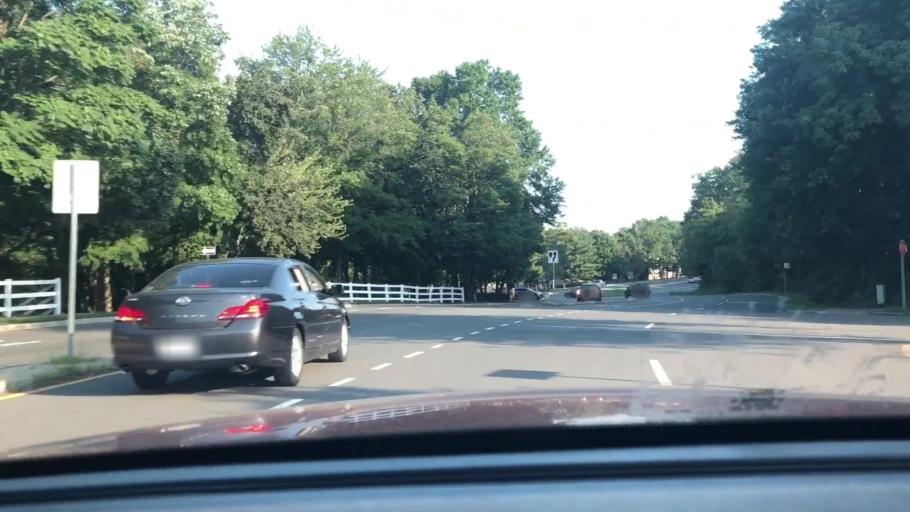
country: US
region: Virginia
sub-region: Fairfax County
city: Centreville
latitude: 38.8381
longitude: -77.4230
